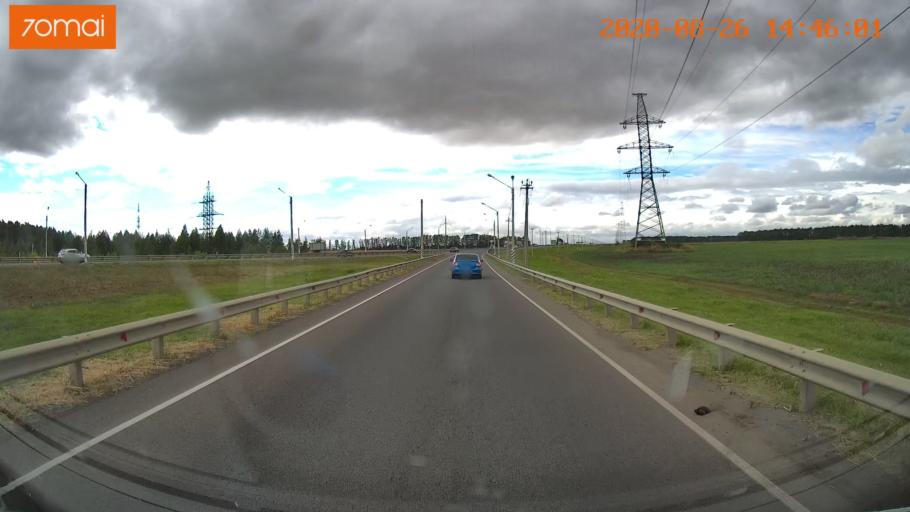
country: RU
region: Rjazan
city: Mikhaylov
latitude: 54.2486
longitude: 39.0505
